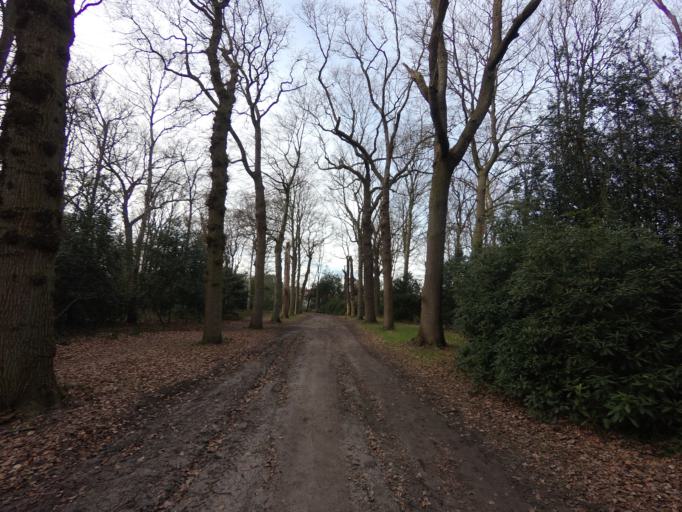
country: NL
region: South Holland
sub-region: Gemeente Teylingen
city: Sassenheim
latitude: 52.2054
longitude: 4.5111
